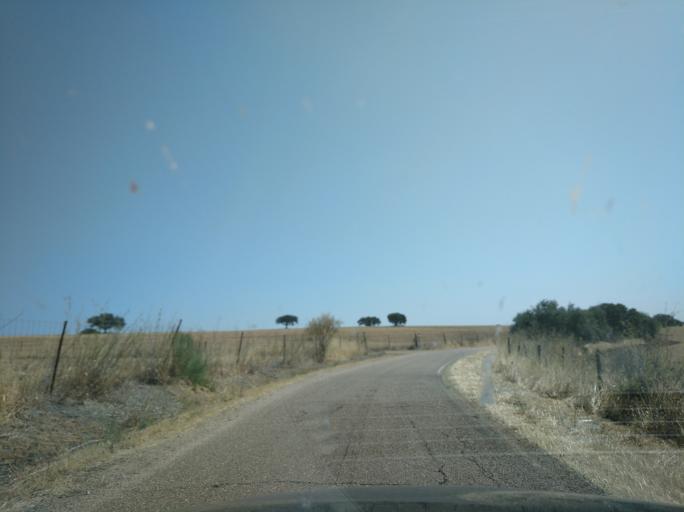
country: PT
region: Portalegre
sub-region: Campo Maior
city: Campo Maior
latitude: 39.0312
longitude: -7.0072
